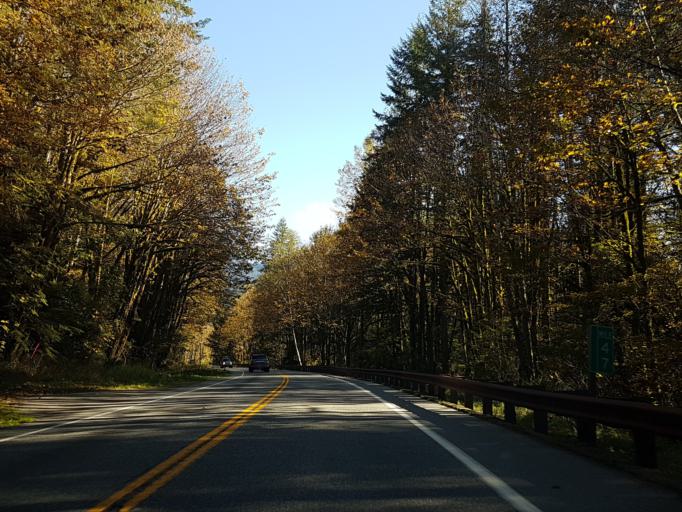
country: US
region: Washington
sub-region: Snohomish County
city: Gold Bar
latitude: 47.7216
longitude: -121.3916
